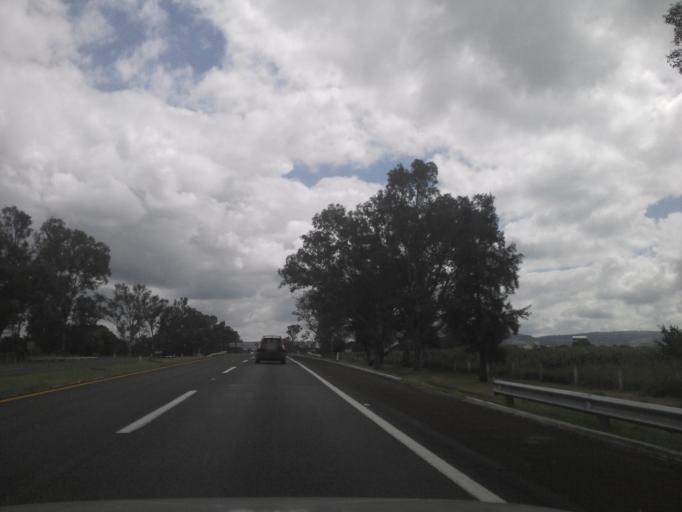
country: MX
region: Jalisco
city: Zapotlanejo
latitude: 20.6150
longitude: -103.0943
